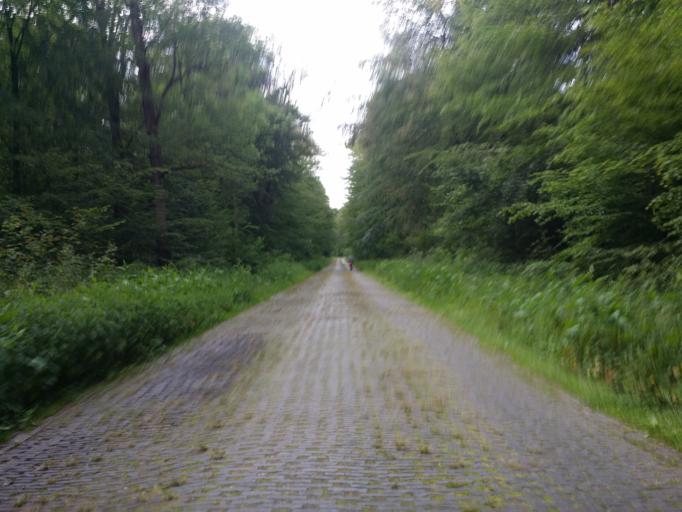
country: DE
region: Lower Saxony
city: Zetel
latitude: 53.3772
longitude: 7.9808
